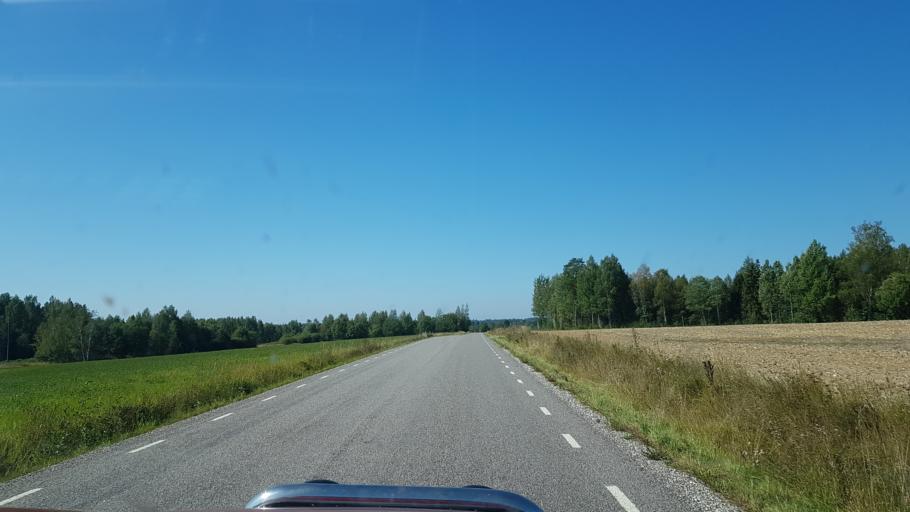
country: EE
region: Polvamaa
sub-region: Polva linn
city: Polva
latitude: 58.2096
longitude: 27.1289
